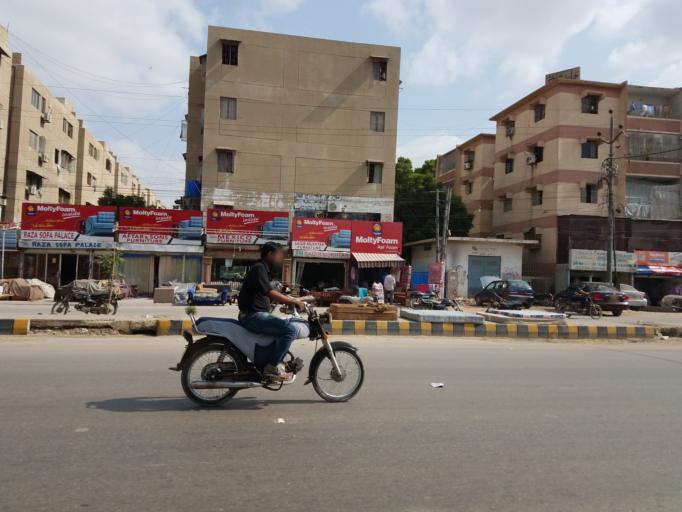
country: PK
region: Sindh
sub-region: Karachi District
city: Karachi
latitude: 24.9298
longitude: 67.0672
